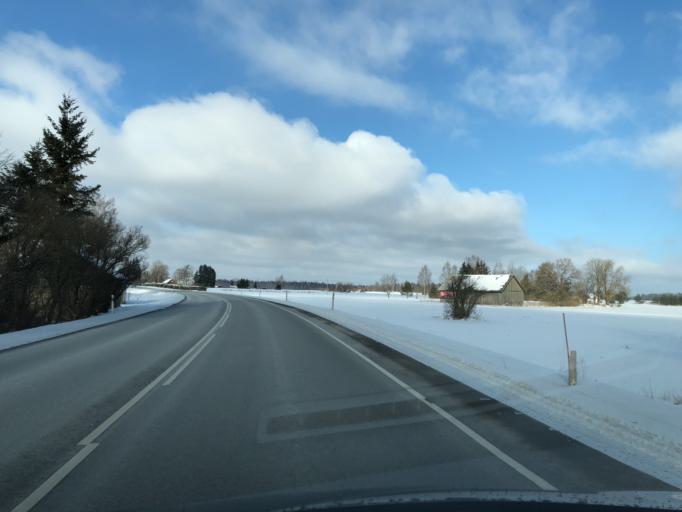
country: EE
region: Jaervamaa
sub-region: Paide linn
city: Paide
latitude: 58.8716
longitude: 25.7022
